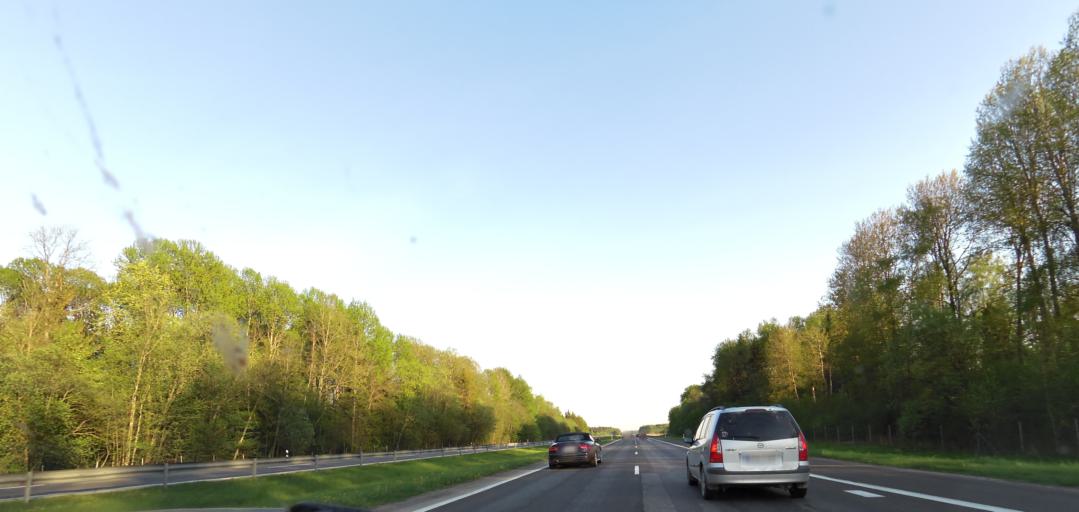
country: LT
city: Sirvintos
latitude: 55.0060
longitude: 24.9189
